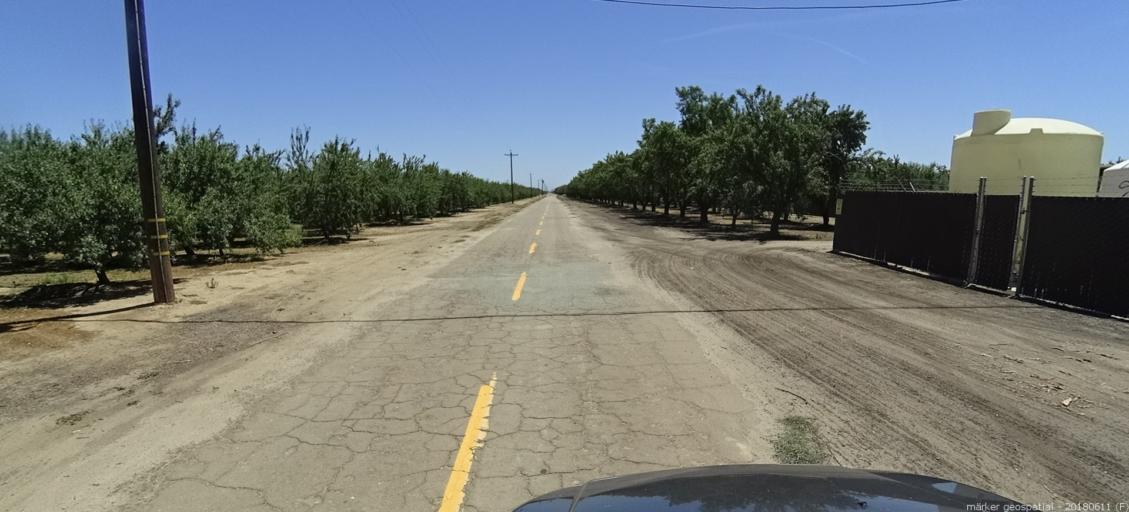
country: US
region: California
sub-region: Madera County
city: Fairmead
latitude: 37.0546
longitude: -120.2068
